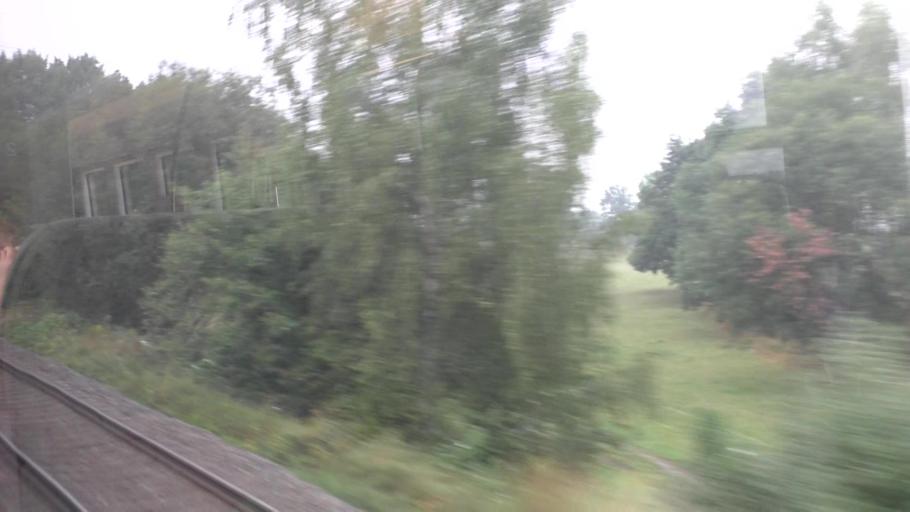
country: DE
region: Saxony
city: Arnsdorf
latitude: 51.0961
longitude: 13.9723
